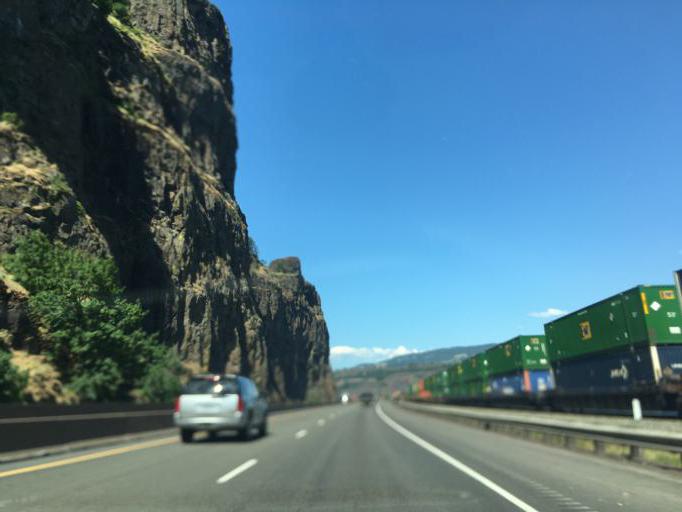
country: US
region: Oregon
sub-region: Wasco County
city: Chenoweth
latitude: 45.6880
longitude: -121.2994
